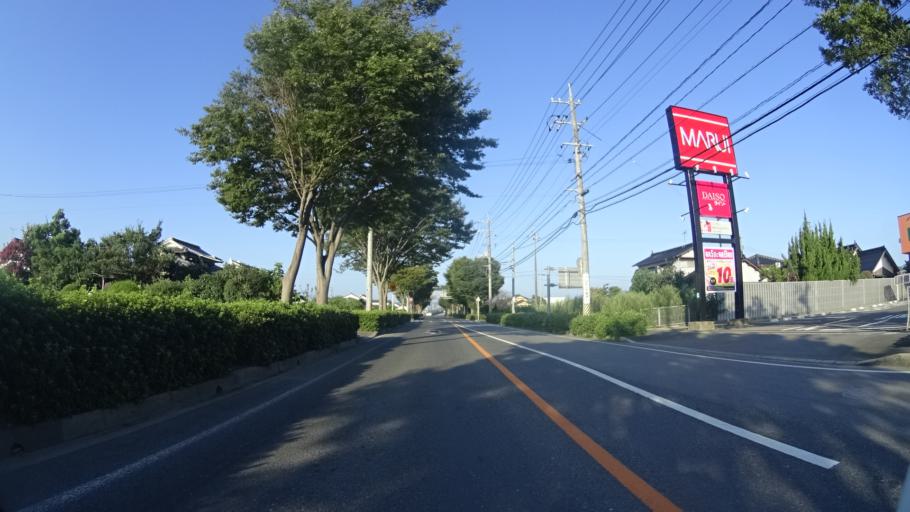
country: JP
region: Shimane
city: Sakaiminato
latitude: 35.5221
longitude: 133.2127
